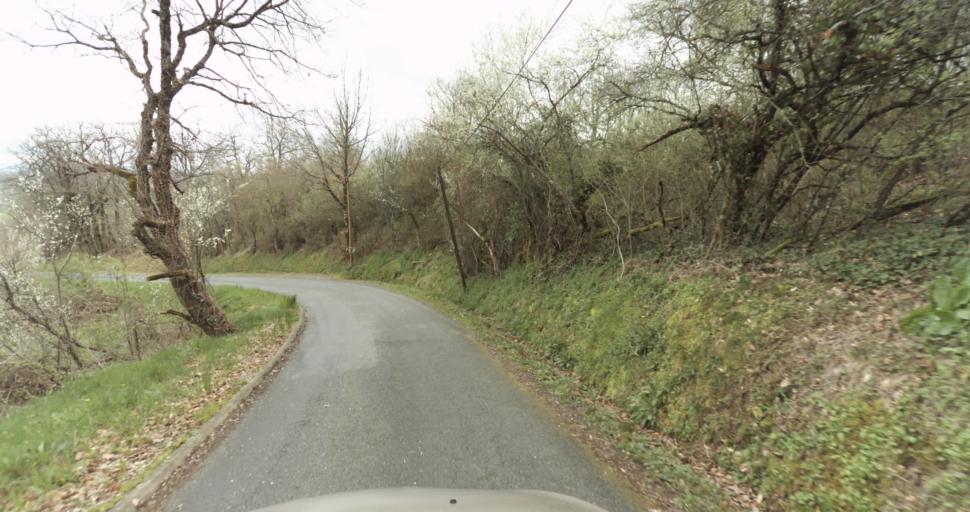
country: FR
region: Midi-Pyrenees
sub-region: Departement du Tarn
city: Frejairolles
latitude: 43.8669
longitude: 2.2056
